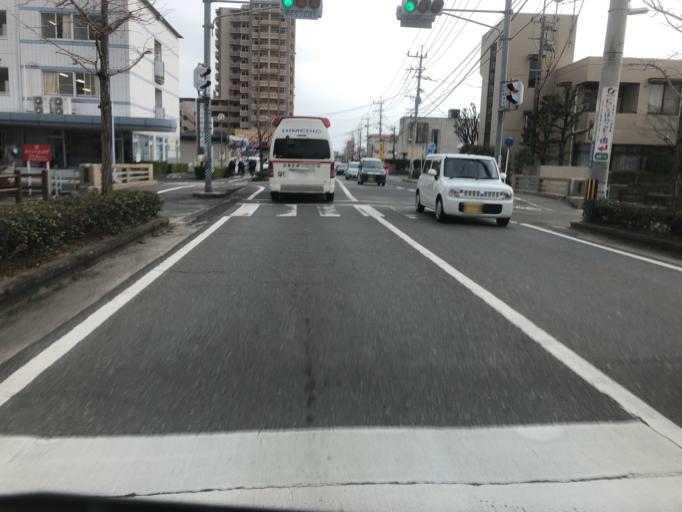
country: JP
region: Saga Prefecture
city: Saga-shi
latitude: 33.2763
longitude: 130.2705
